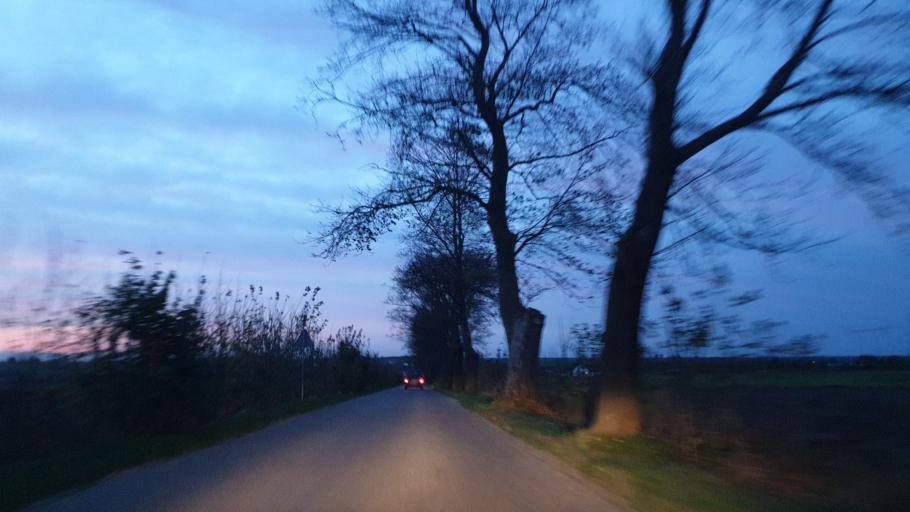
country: PL
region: Pomeranian Voivodeship
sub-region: Powiat pucki
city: Krokowa
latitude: 54.7799
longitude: 18.2035
